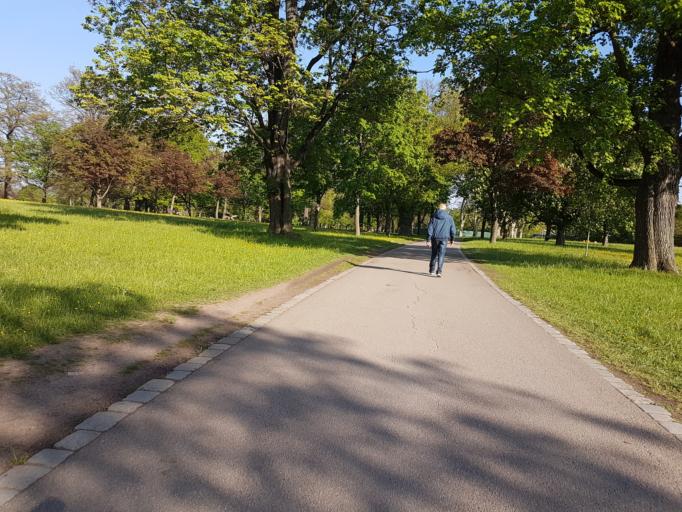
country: DE
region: Baden-Wuerttemberg
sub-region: Regierungsbezirk Stuttgart
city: Stuttgart-Ost
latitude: 48.8025
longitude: 9.1983
